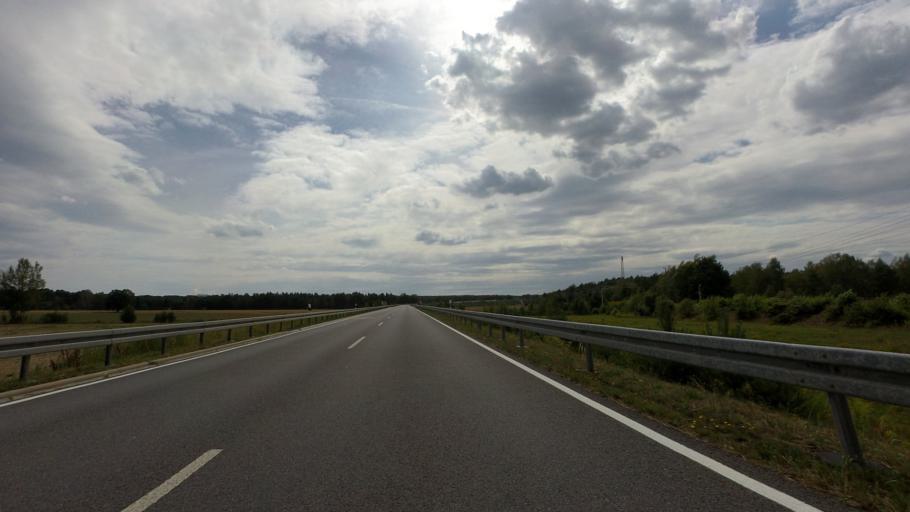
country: DE
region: Brandenburg
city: Spremberg
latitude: 51.5896
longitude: 14.3527
